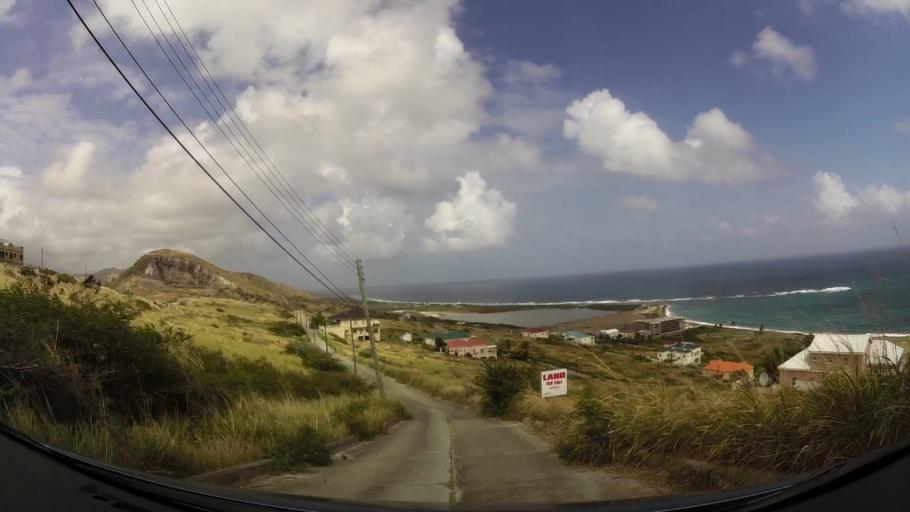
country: KN
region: Saint Peter Basseterre
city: Monkey Hill
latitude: 17.3033
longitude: -62.6954
